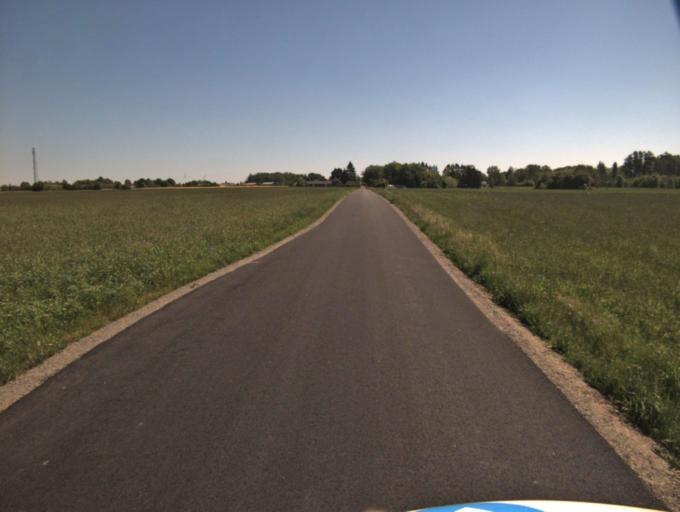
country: SE
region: Skane
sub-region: Kristianstads Kommun
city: Kristianstad
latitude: 56.0161
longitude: 14.2102
